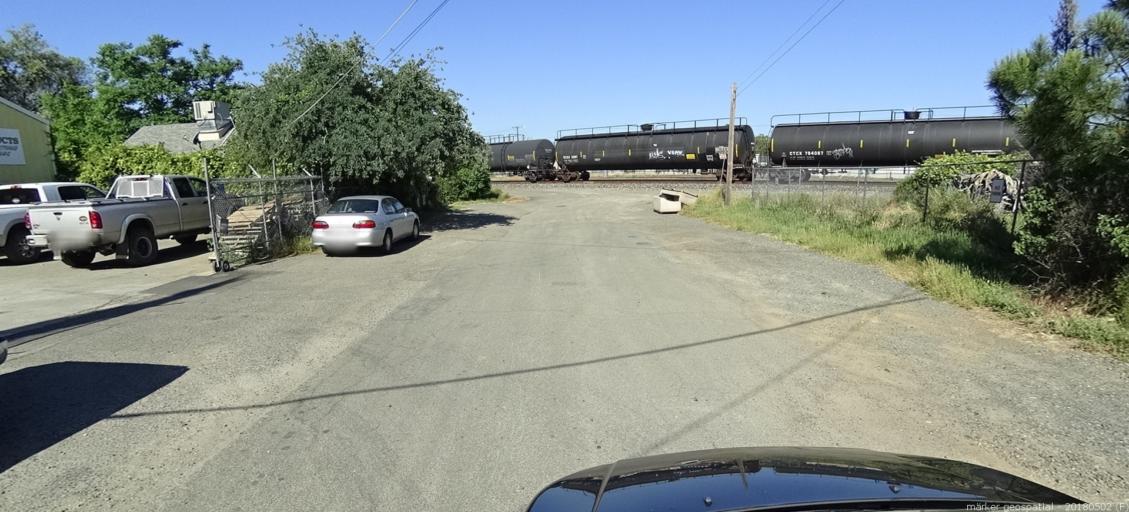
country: US
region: California
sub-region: Sacramento County
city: Arden-Arcade
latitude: 38.6095
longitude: -121.4363
